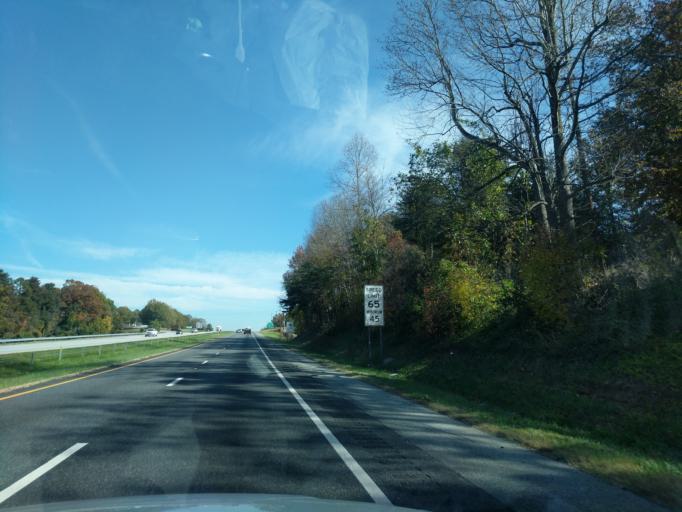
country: US
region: South Carolina
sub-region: Cherokee County
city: Blacksburg
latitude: 35.1447
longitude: -81.5005
